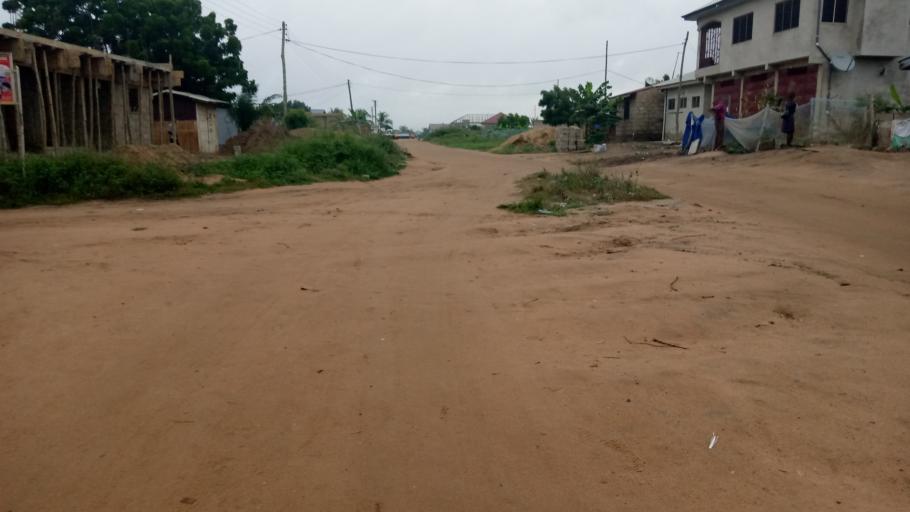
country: GH
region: Central
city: Kasoa
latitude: 5.4991
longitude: -0.4090
